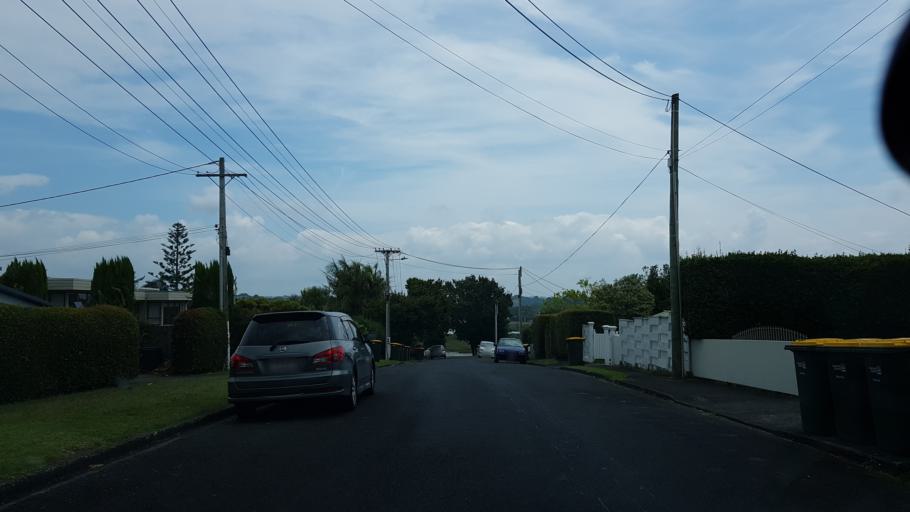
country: NZ
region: Auckland
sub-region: Auckland
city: North Shore
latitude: -36.8009
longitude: 174.7700
